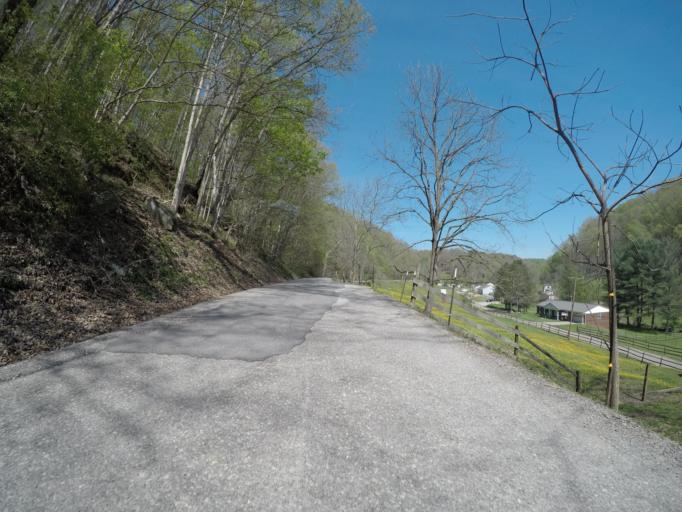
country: US
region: West Virginia
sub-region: Kanawha County
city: Charleston
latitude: 38.4142
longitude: -81.6181
